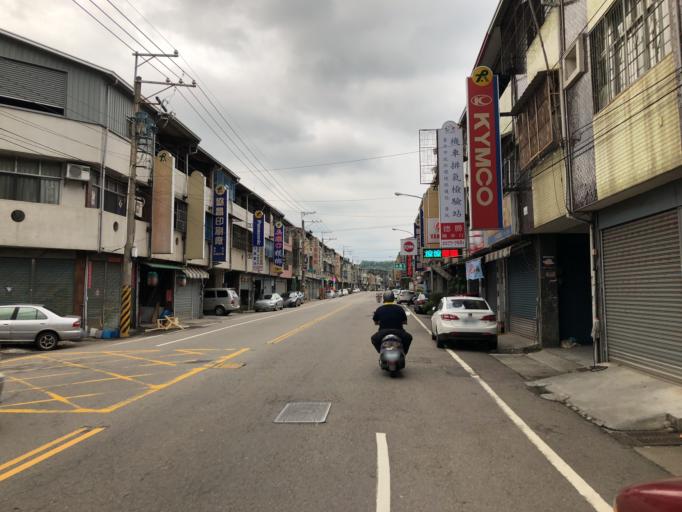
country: TW
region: Taiwan
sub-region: Taichung City
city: Taichung
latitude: 24.1234
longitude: 120.7345
